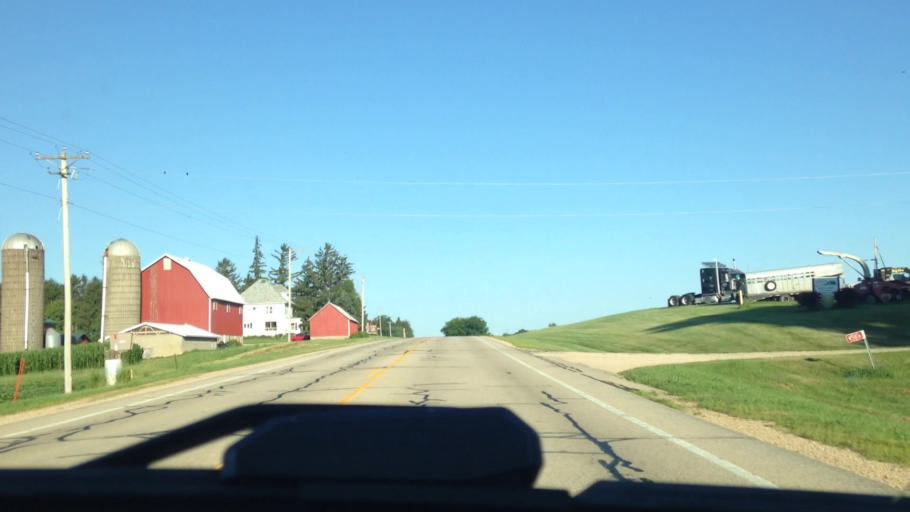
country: US
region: Wisconsin
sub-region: Dane County
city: De Forest
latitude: 43.3324
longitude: -89.2903
